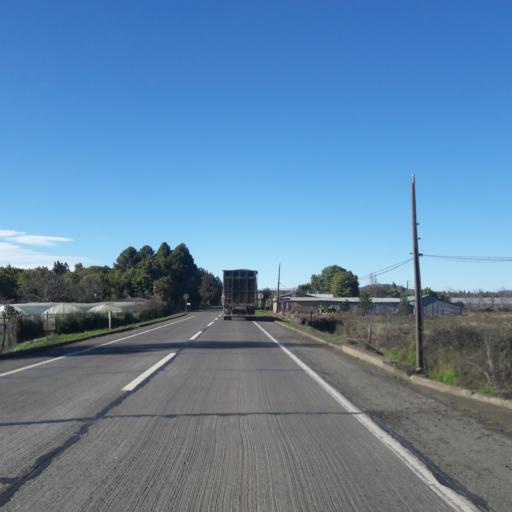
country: CL
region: Araucania
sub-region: Provincia de Malleco
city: Angol
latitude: -37.7758
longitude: -72.5429
